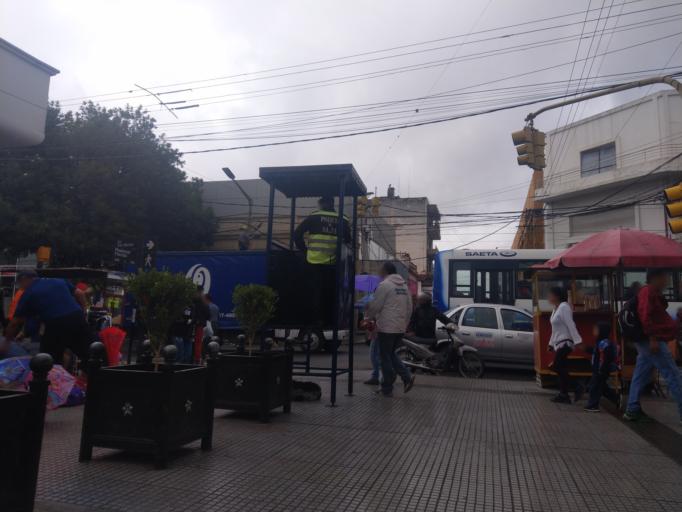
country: AR
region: Salta
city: Salta
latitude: -24.7932
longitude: -65.4128
